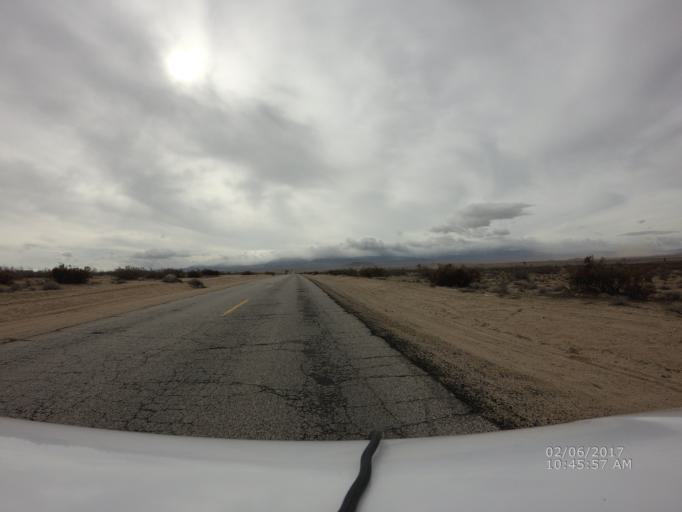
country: US
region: California
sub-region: Los Angeles County
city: Lake Los Angeles
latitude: 34.6322
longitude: -117.7027
